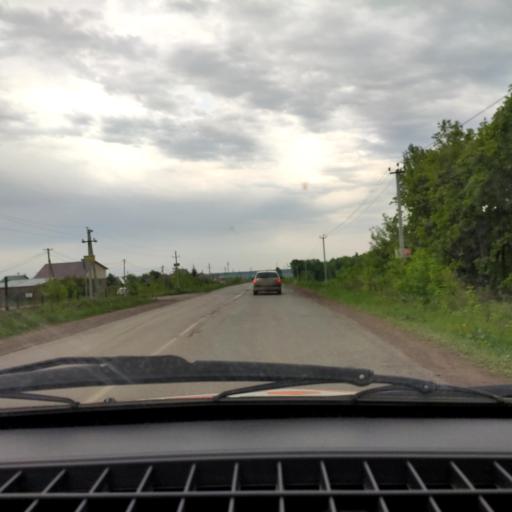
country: RU
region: Bashkortostan
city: Avdon
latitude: 54.5787
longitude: 55.7518
